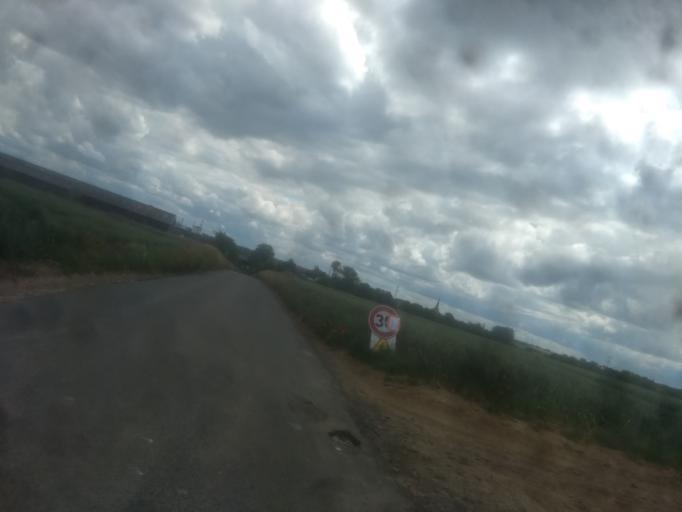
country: FR
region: Nord-Pas-de-Calais
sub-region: Departement du Pas-de-Calais
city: Agny
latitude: 50.2310
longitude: 2.7337
